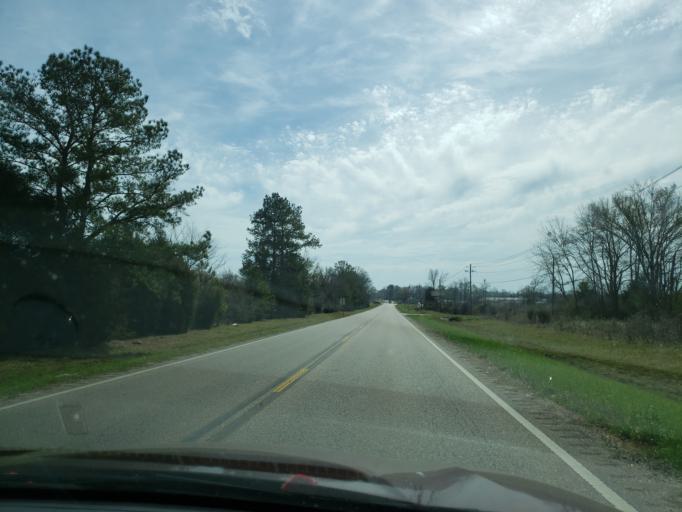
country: US
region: Alabama
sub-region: Dallas County
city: Selma
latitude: 32.4385
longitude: -87.0646
